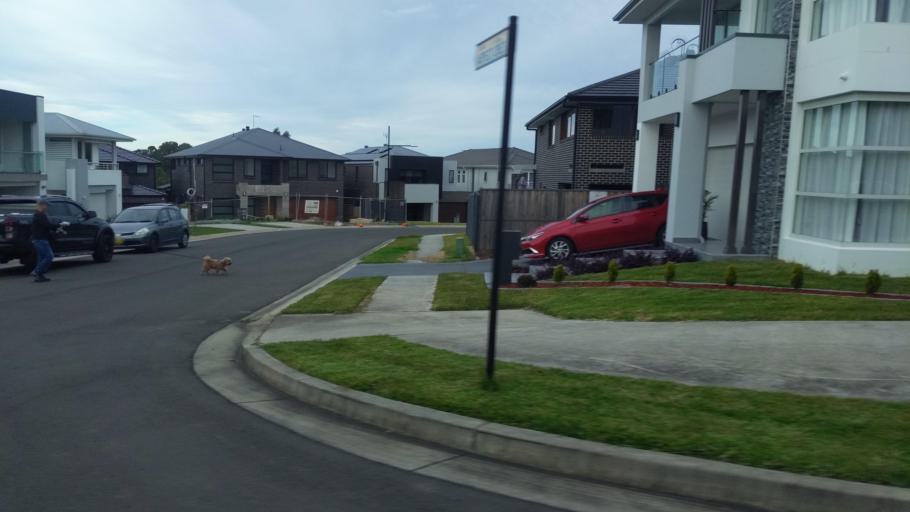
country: AU
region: New South Wales
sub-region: Blacktown
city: Quakers Hill
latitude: -33.7243
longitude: 150.8638
